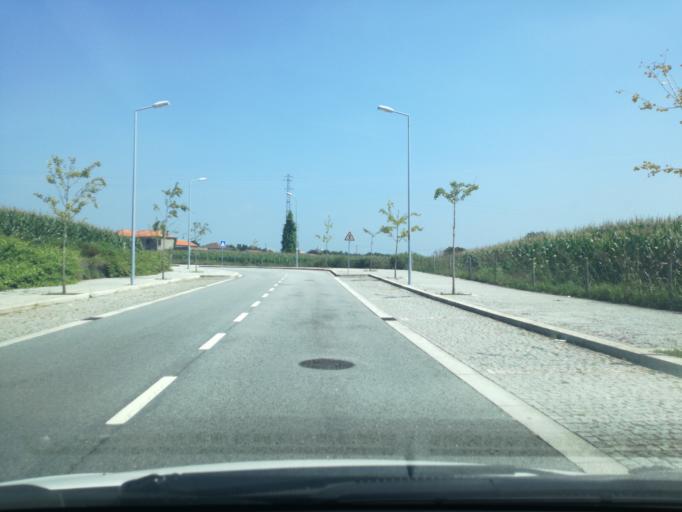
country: PT
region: Porto
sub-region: Maia
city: Gemunde
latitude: 41.2461
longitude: -8.6589
